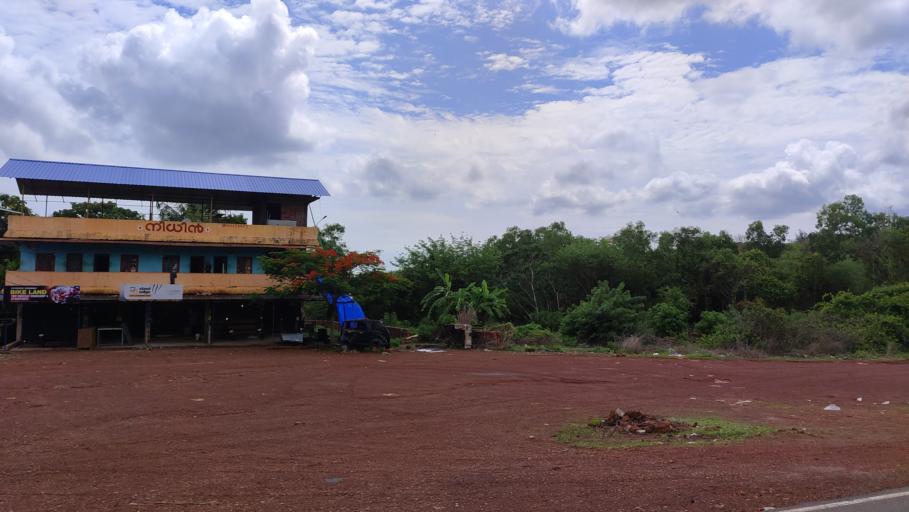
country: IN
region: Kerala
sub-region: Kasaragod District
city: Kannangad
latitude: 12.3914
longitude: 75.1011
